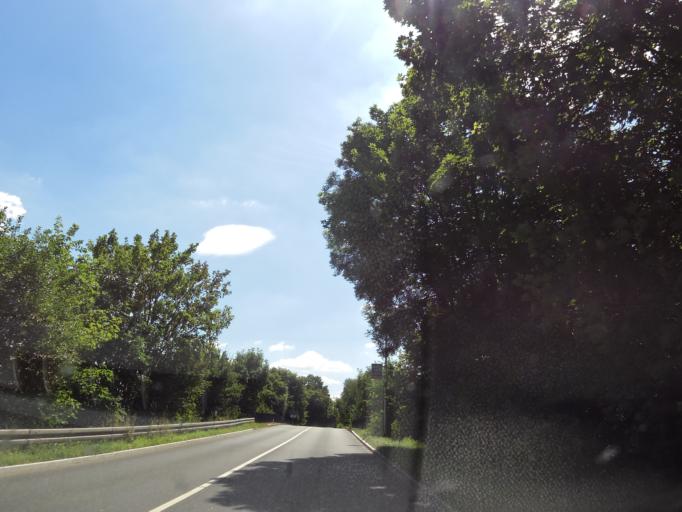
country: DE
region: Saxony
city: Glauchau
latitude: 50.8308
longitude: 12.5212
